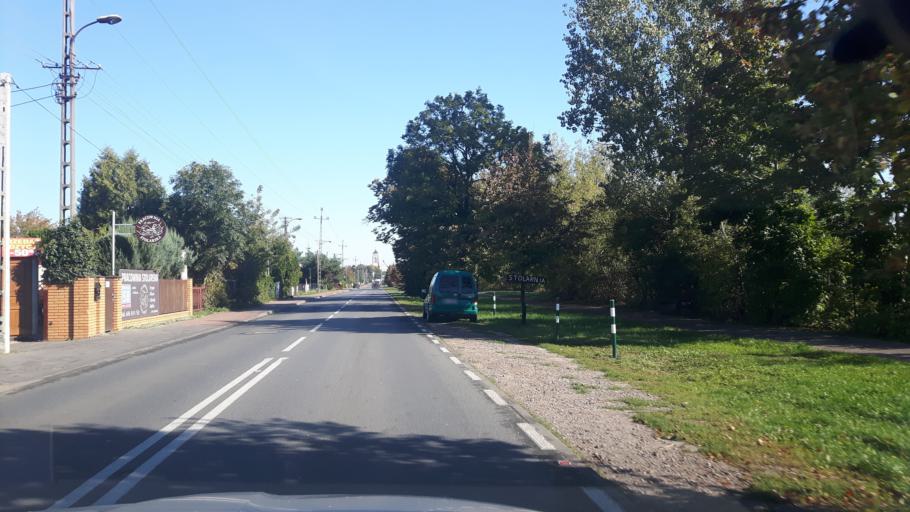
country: PL
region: Masovian Voivodeship
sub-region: Powiat legionowski
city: Wieliszew
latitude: 52.4446
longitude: 20.9651
